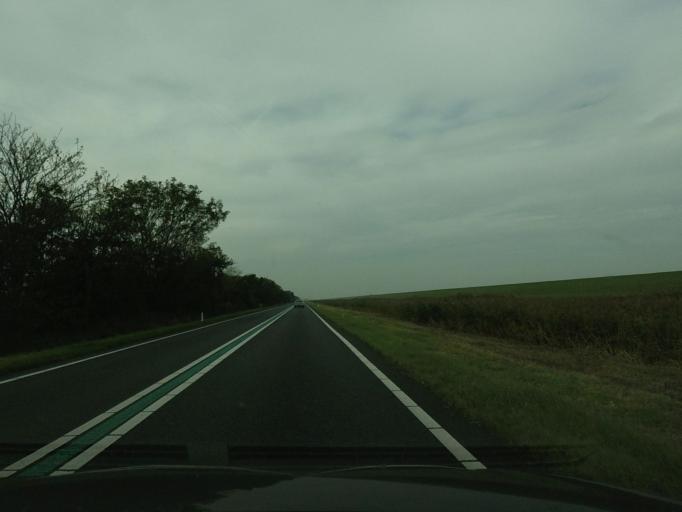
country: NL
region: North Holland
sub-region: Gemeente Schagen
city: Schagen
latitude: 52.8894
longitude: 4.8643
